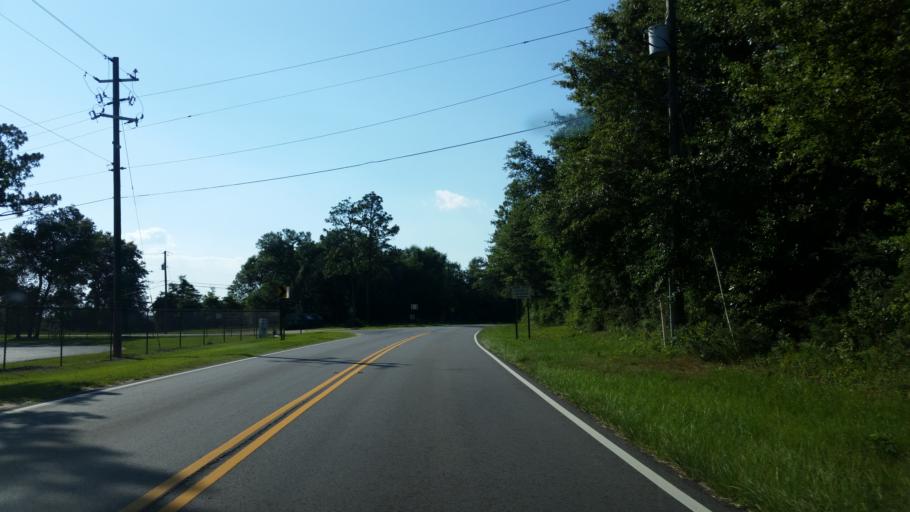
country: US
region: Florida
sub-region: Escambia County
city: Cantonment
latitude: 30.5793
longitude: -87.3964
